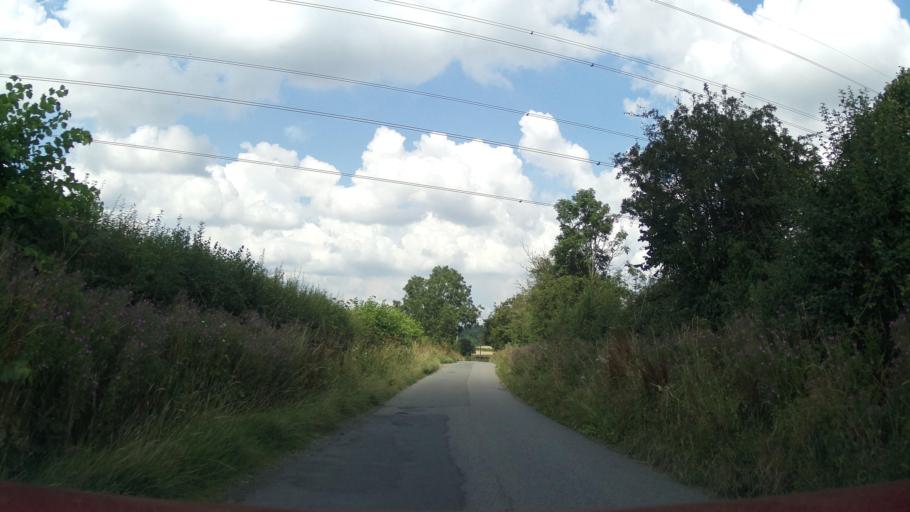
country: GB
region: England
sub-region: Wiltshire
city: Hankerton
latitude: 51.5871
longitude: -2.0181
